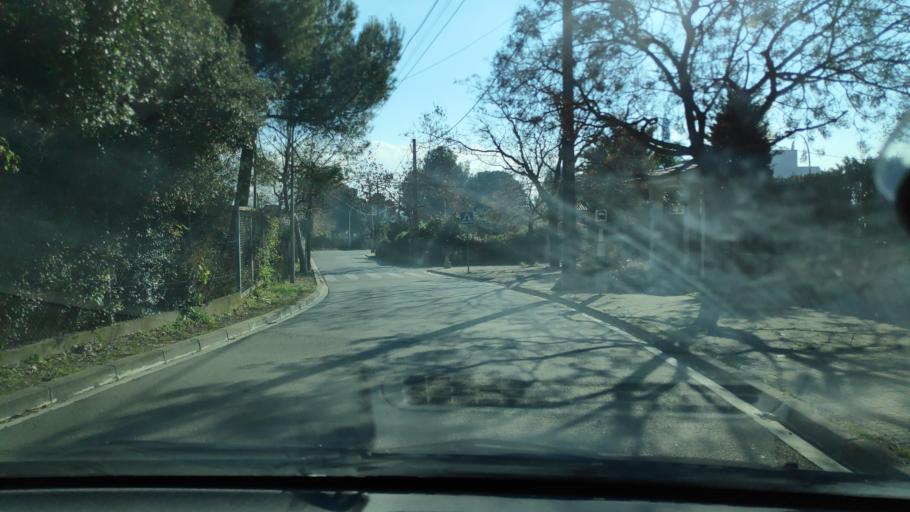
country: ES
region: Catalonia
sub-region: Provincia de Barcelona
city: Sant Cugat del Valles
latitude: 41.4981
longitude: 2.0809
